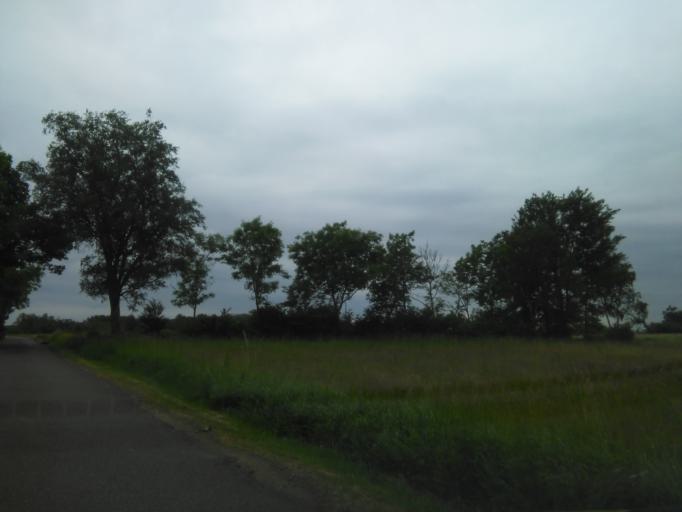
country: DK
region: Capital Region
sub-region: Bornholm Kommune
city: Akirkeby
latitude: 55.0937
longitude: 14.8808
